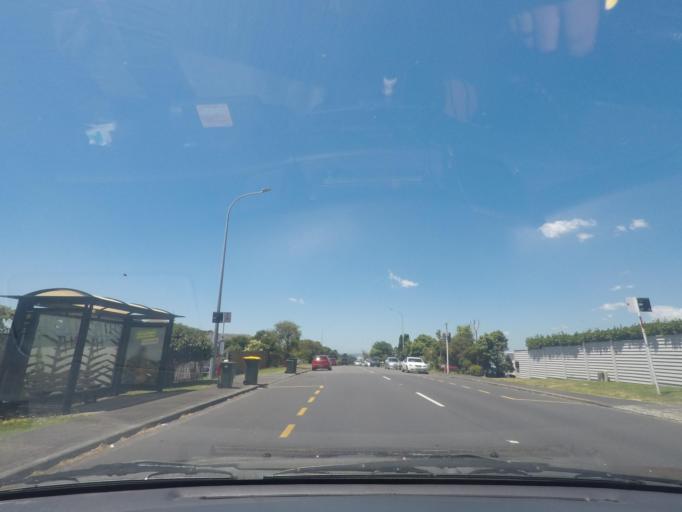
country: NZ
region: Auckland
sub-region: Auckland
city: Mangere
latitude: -36.9303
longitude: 174.7429
